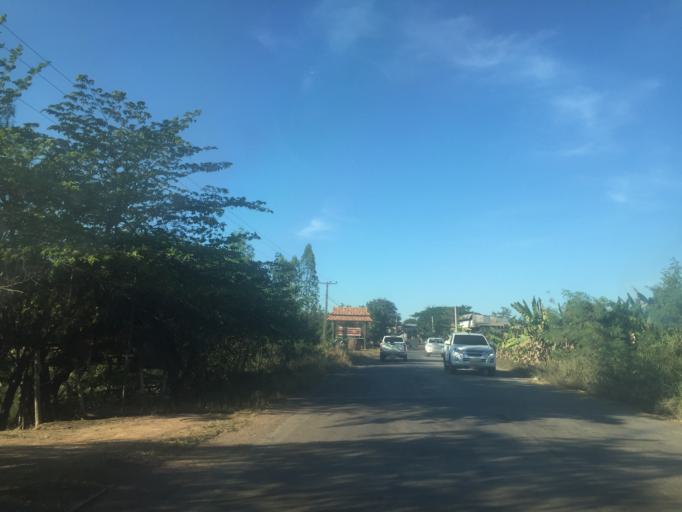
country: TH
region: Kalasin
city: Tha Khantho
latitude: 16.9757
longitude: 103.2617
